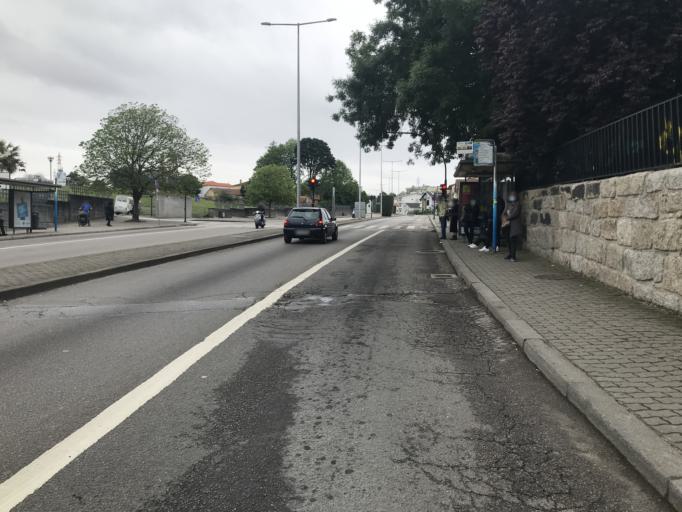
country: PT
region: Porto
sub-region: Matosinhos
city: Senhora da Hora
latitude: 41.1806
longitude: -8.6640
